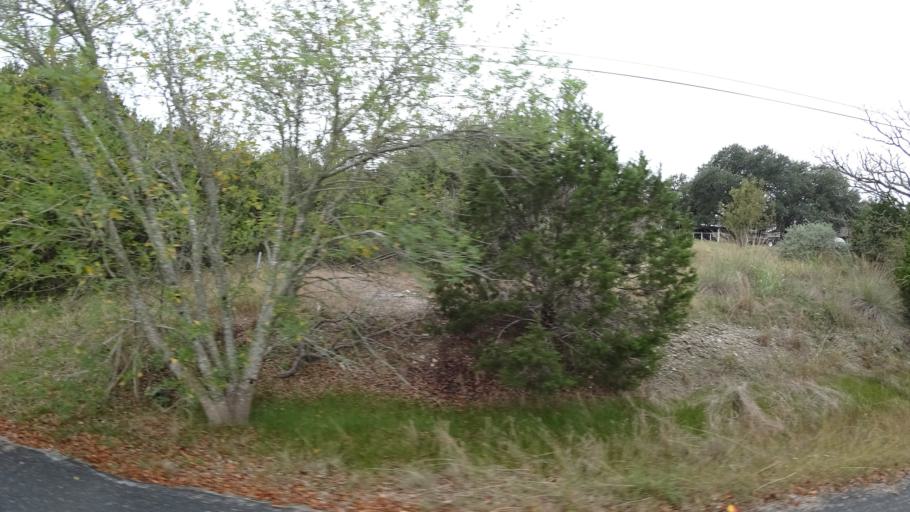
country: US
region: Texas
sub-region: Travis County
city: Barton Creek
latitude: 30.2340
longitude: -97.8994
